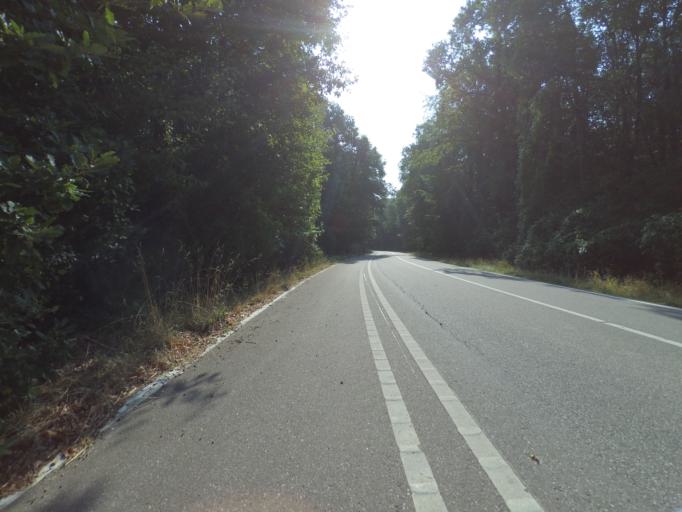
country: LU
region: Grevenmacher
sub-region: Canton de Remich
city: Remich
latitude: 49.5185
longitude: 6.4015
